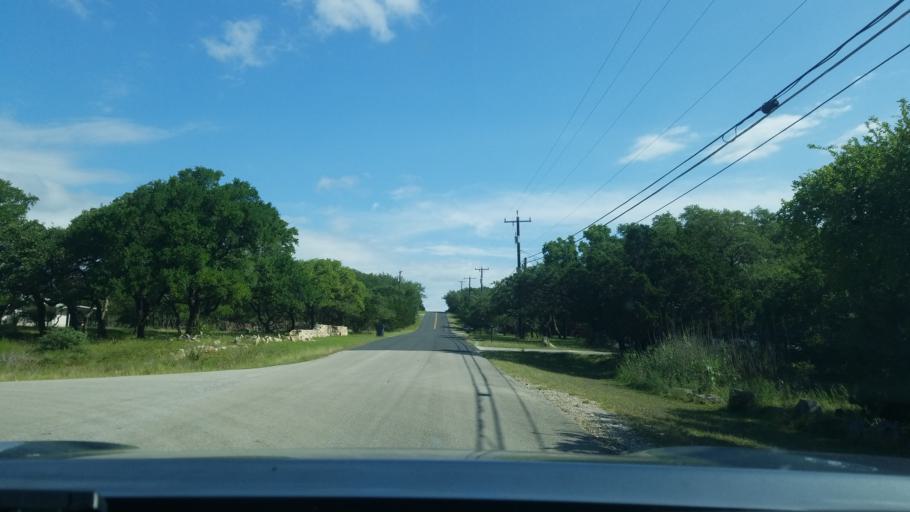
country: US
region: Texas
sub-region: Comal County
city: Bulverde
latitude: 29.7451
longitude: -98.4427
